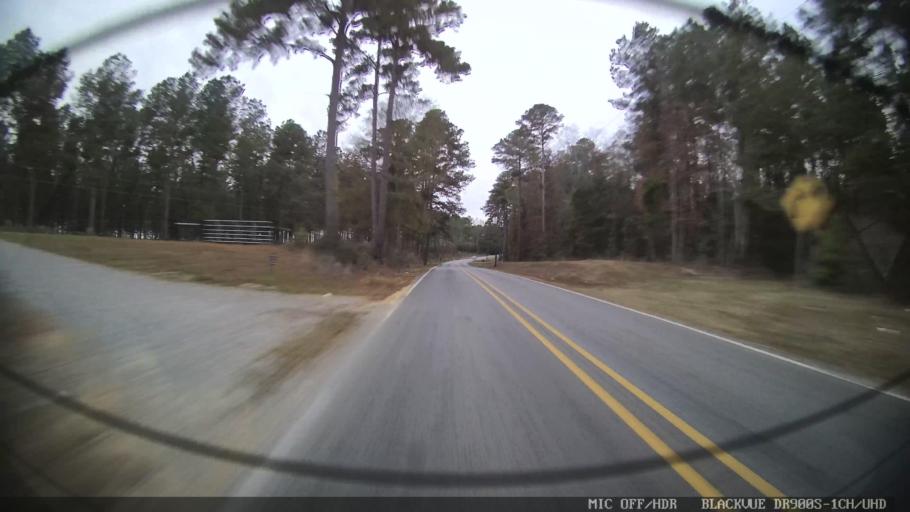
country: US
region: Mississippi
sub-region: Clarke County
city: Quitman
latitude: 32.0287
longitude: -88.8156
